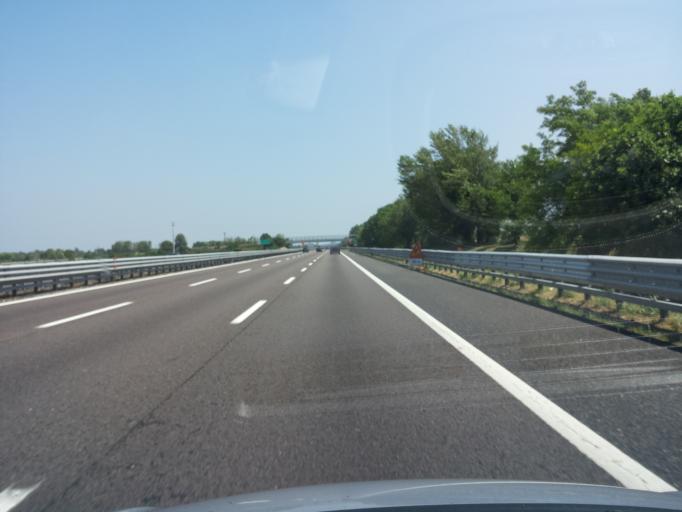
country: IT
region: Lombardy
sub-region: Provincia di Brescia
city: Desenzano del Garda
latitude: 45.4410
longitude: 10.5632
